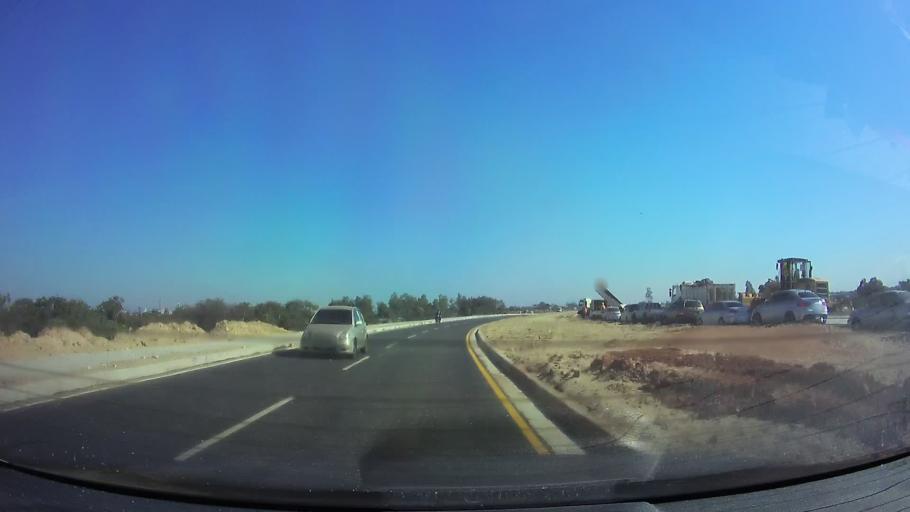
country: PY
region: Asuncion
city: Asuncion
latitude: -25.2485
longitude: -57.5996
